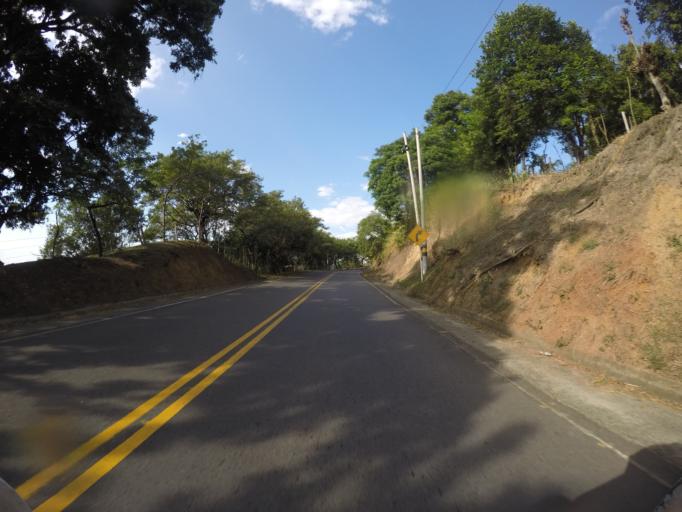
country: CO
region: Valle del Cauca
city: Cartago
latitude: 4.7271
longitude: -75.8770
